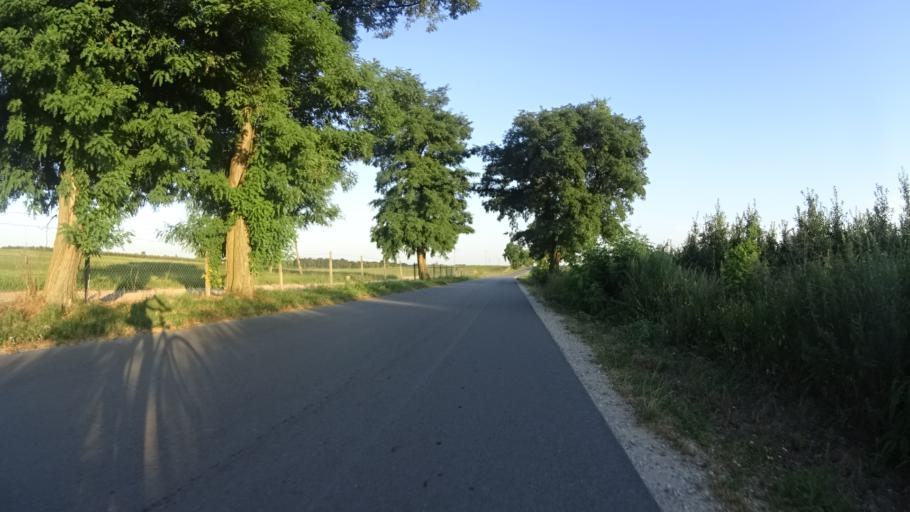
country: PL
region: Masovian Voivodeship
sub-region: Powiat grojecki
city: Goszczyn
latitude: 51.6846
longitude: 20.8230
